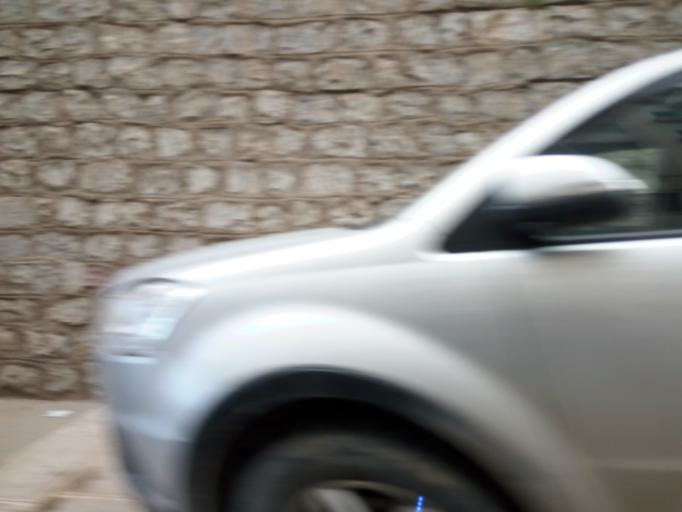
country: DZ
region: Constantine
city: Constantine
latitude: 36.3591
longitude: 6.6077
